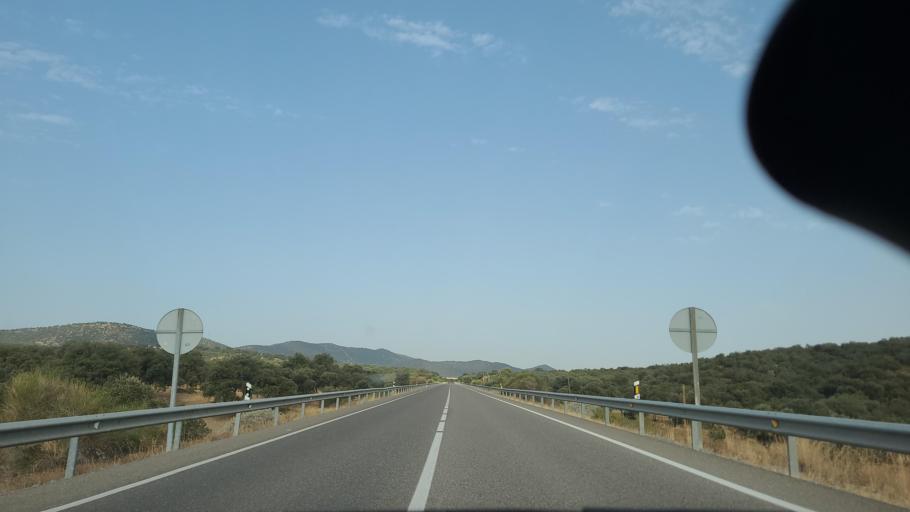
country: ES
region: Andalusia
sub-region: Province of Cordoba
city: Espiel
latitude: 38.2022
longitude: -5.1082
